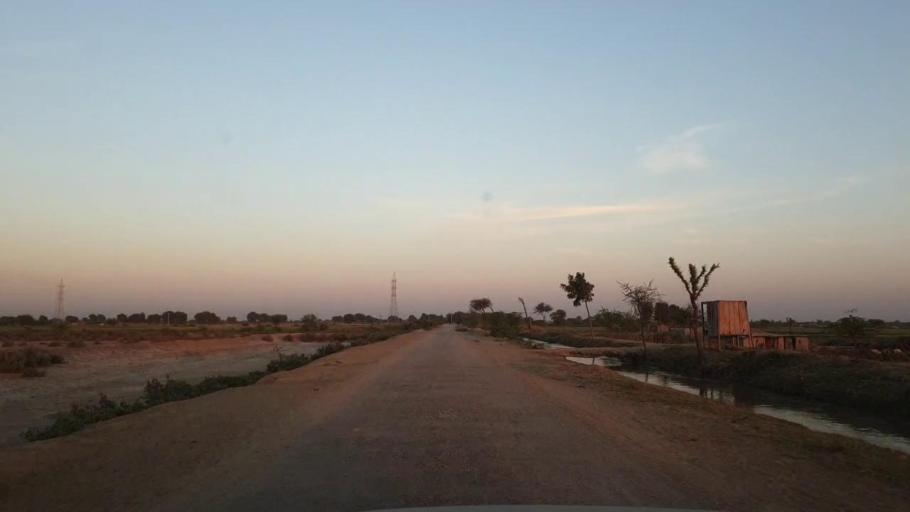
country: PK
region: Sindh
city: Kunri
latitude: 25.1469
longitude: 69.4400
